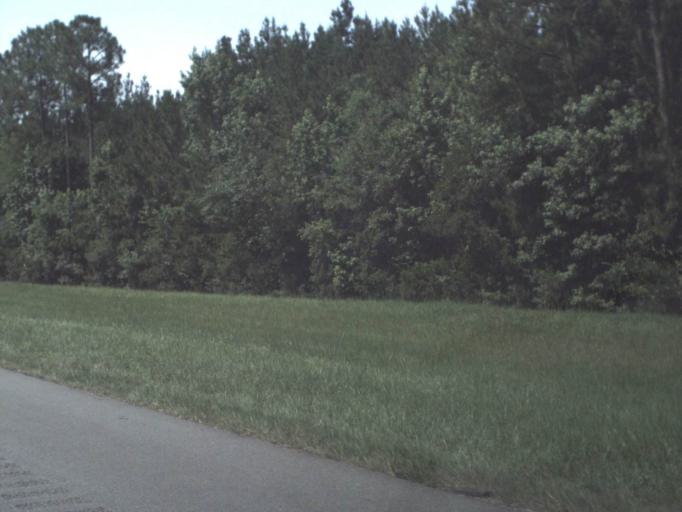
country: US
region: Florida
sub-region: Nassau County
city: Yulee
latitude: 30.6431
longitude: -81.6585
